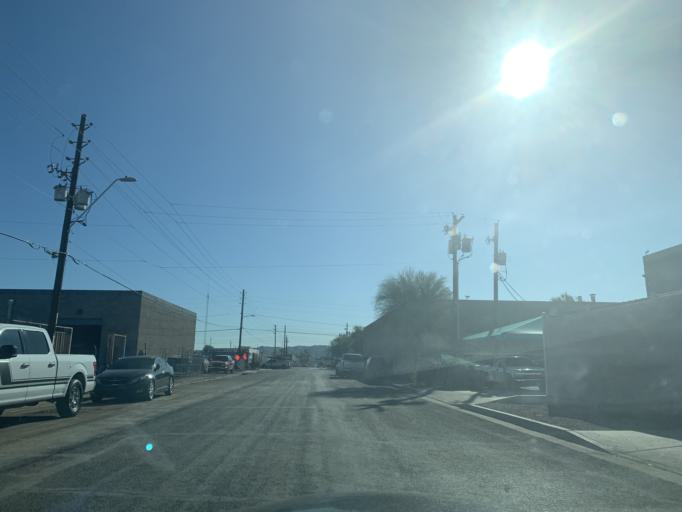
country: US
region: Arizona
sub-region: Maricopa County
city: Tempe Junction
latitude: 33.4172
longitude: -111.9998
